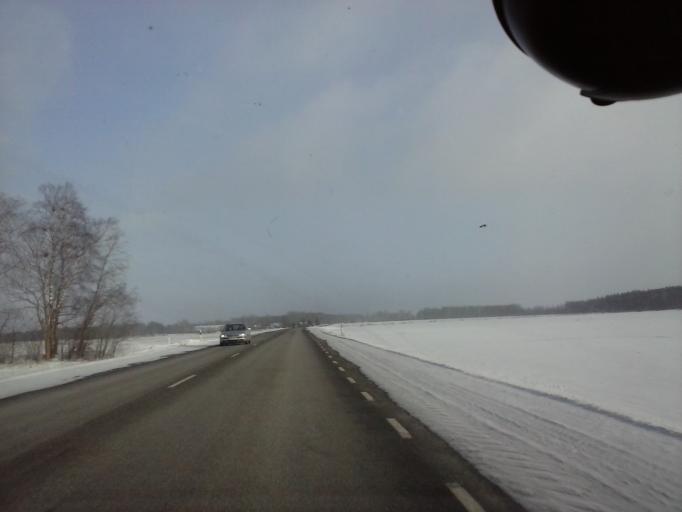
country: EE
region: Tartu
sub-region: Puhja vald
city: Puhja
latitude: 58.3302
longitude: 26.1949
